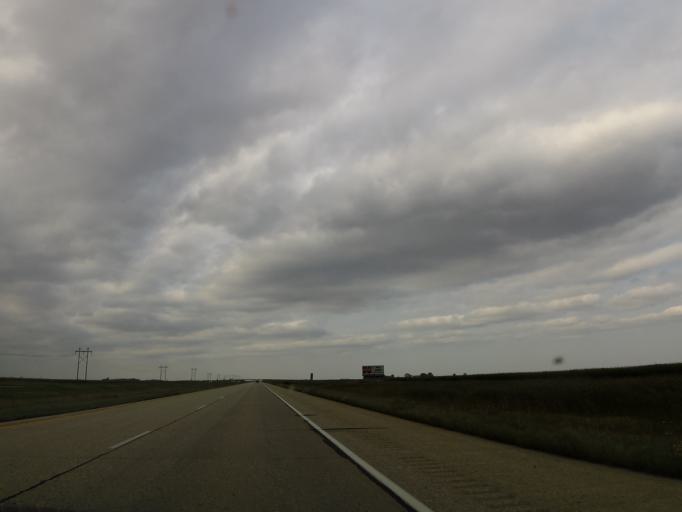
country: US
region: North Dakota
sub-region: Richland County
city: Wahpeton
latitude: 46.2087
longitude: -96.8340
